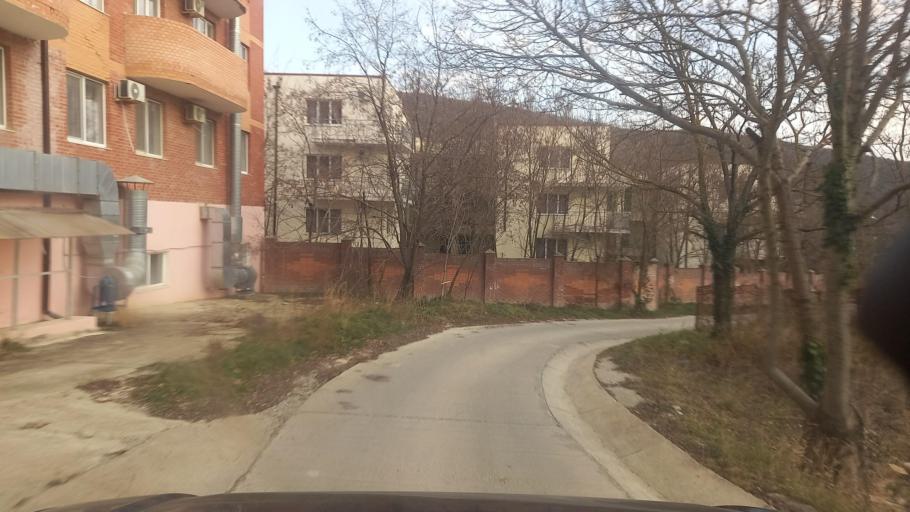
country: RU
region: Krasnodarskiy
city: Myskhako
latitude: 44.6663
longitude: 37.6817
